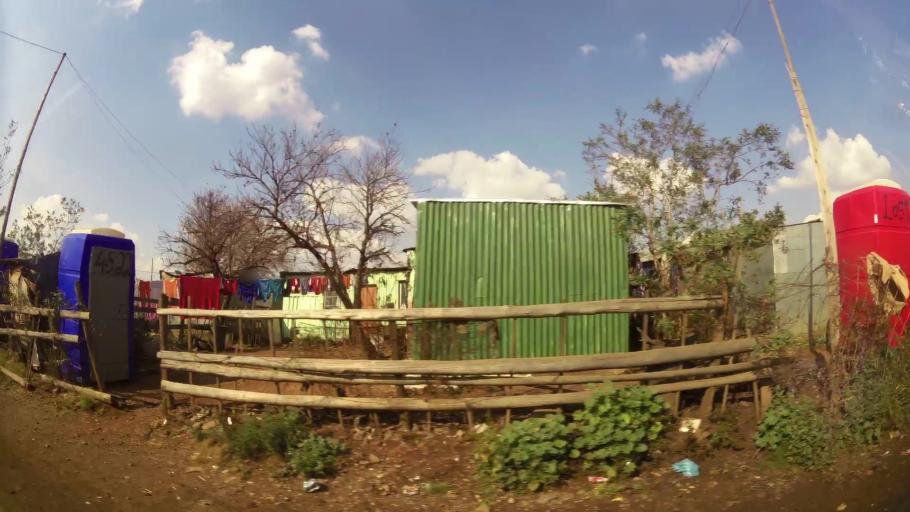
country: ZA
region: Gauteng
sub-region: Ekurhuleni Metropolitan Municipality
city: Germiston
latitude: -26.3318
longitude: 28.1406
